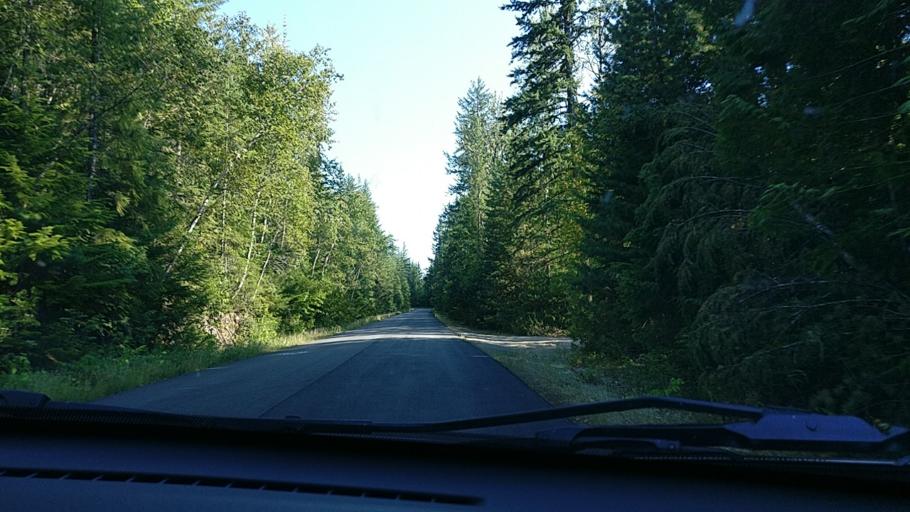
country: CA
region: British Columbia
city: Revelstoke
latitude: 51.0235
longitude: -118.2030
